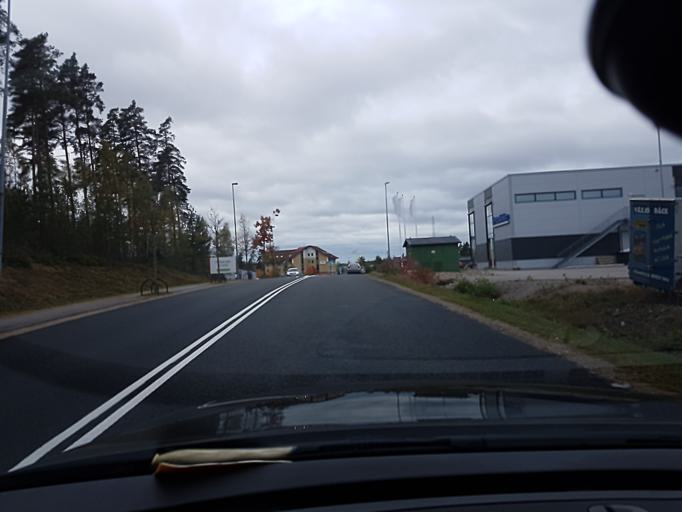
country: SE
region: Kronoberg
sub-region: Vaxjo Kommun
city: Vaexjoe
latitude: 56.9031
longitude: 14.8350
